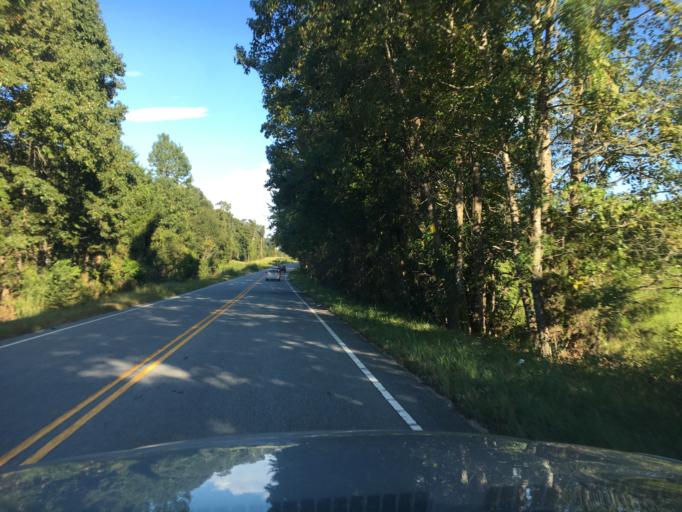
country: US
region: South Carolina
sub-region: Spartanburg County
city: Woodruff
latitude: 34.7898
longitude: -82.1203
